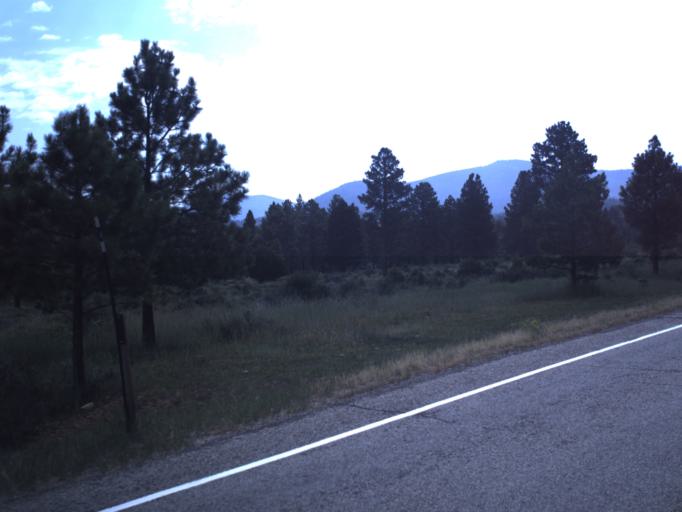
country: US
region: Utah
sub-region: Daggett County
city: Manila
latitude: 40.8682
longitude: -109.4896
